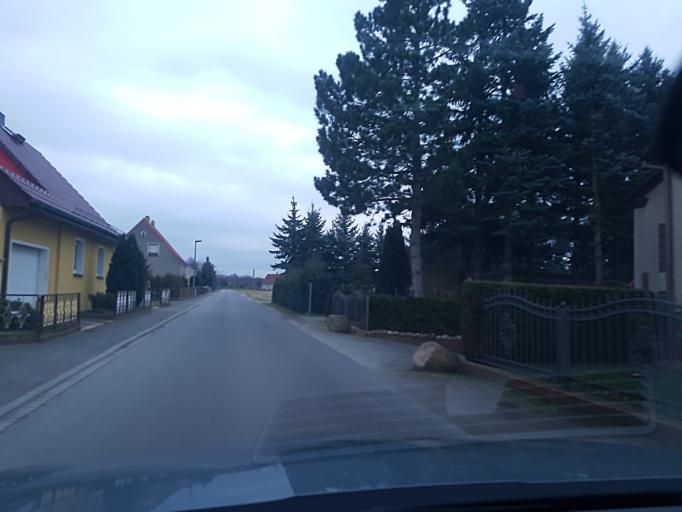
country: DE
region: Brandenburg
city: Doberlug-Kirchhain
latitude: 51.6090
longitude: 13.5590
